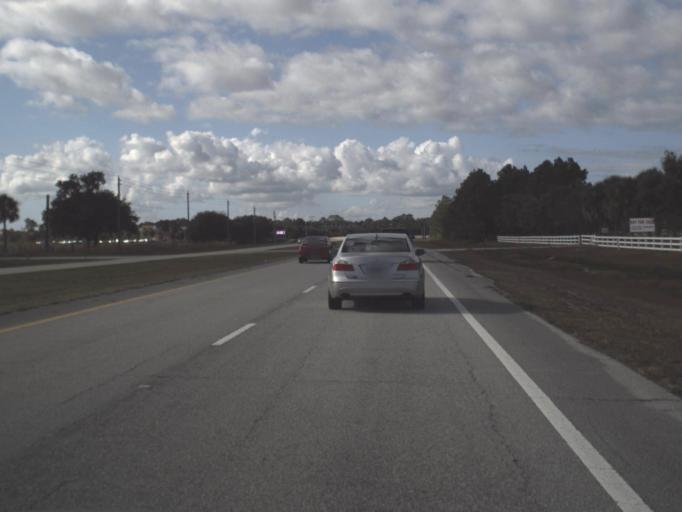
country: US
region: Florida
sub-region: Volusia County
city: Daytona Beach
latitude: 29.1650
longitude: -81.0732
